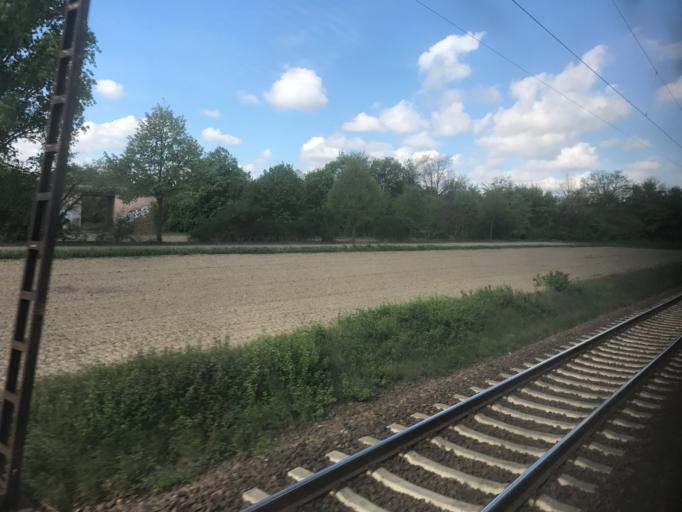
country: DE
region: Rheinland-Pfalz
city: Frankenthal
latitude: 49.5038
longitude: 8.3575
